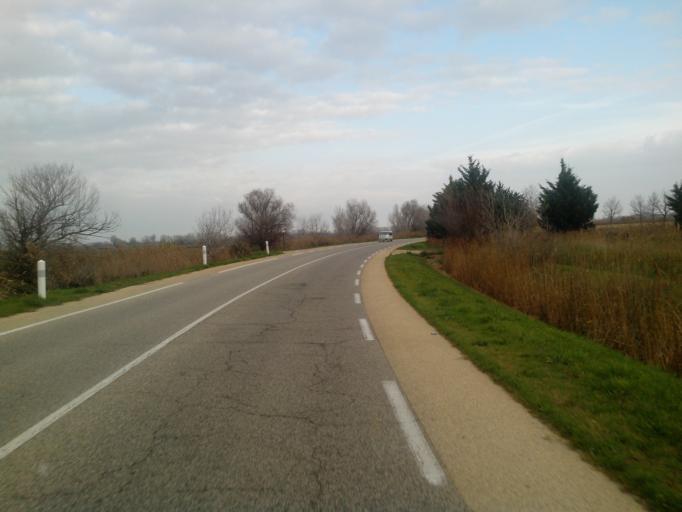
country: FR
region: Languedoc-Roussillon
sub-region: Departement du Gard
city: Saint-Gilles
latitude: 43.5736
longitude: 4.4217
